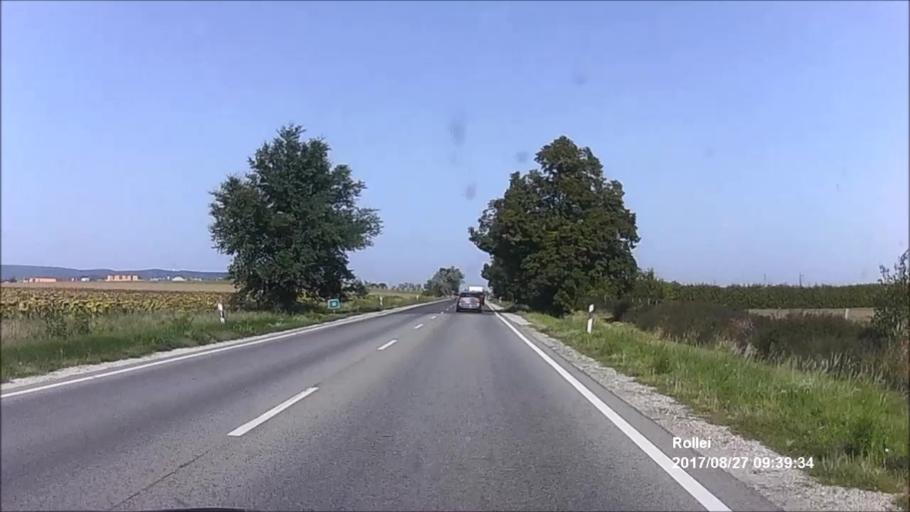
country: AT
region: Burgenland
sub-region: Politischer Bezirk Oberpullendorf
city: Deutschkreutz
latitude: 47.6312
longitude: 16.6579
